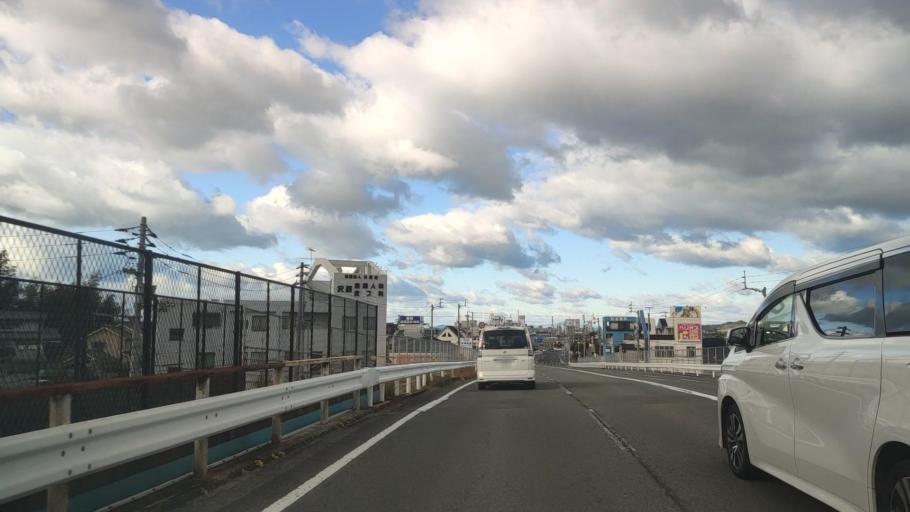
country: JP
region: Ehime
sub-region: Shikoku-chuo Shi
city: Matsuyama
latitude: 33.8565
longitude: 132.7290
